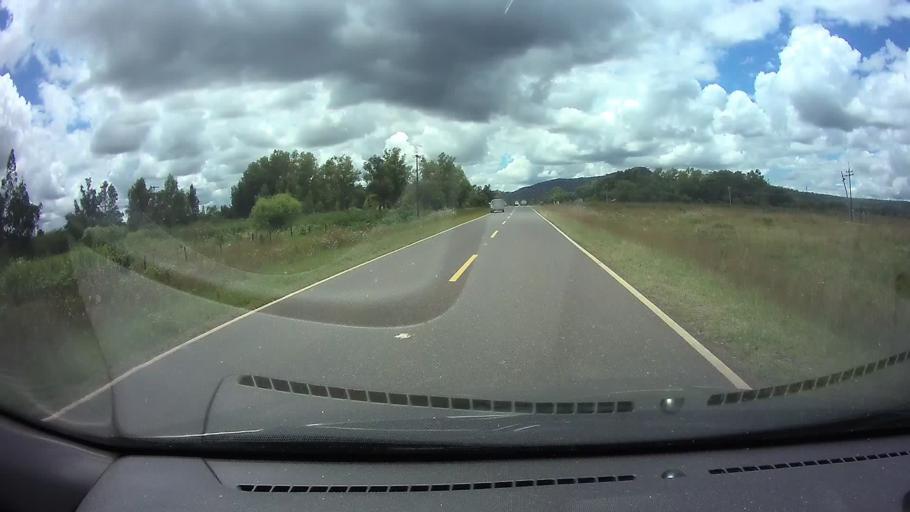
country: PY
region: Paraguari
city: Ybycui
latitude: -25.9099
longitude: -57.0049
